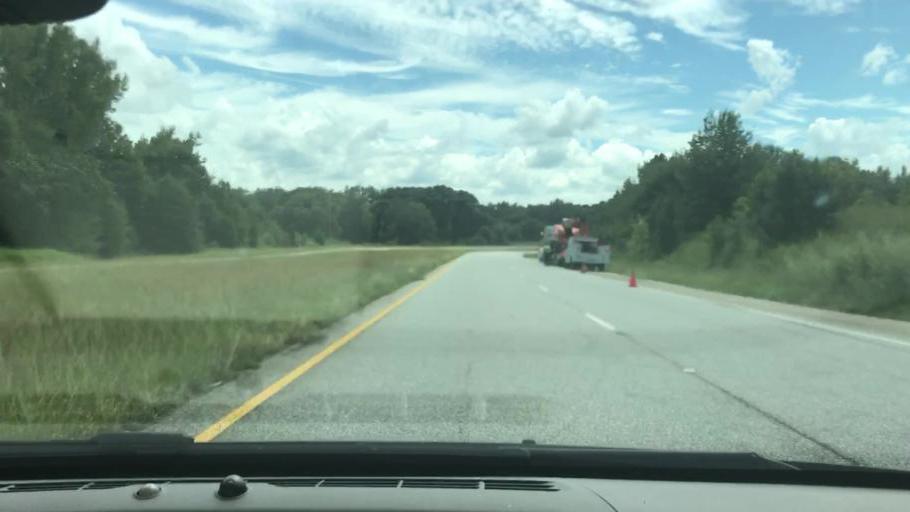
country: US
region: Georgia
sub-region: Stewart County
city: Lumpkin
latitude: 32.1596
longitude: -84.8301
